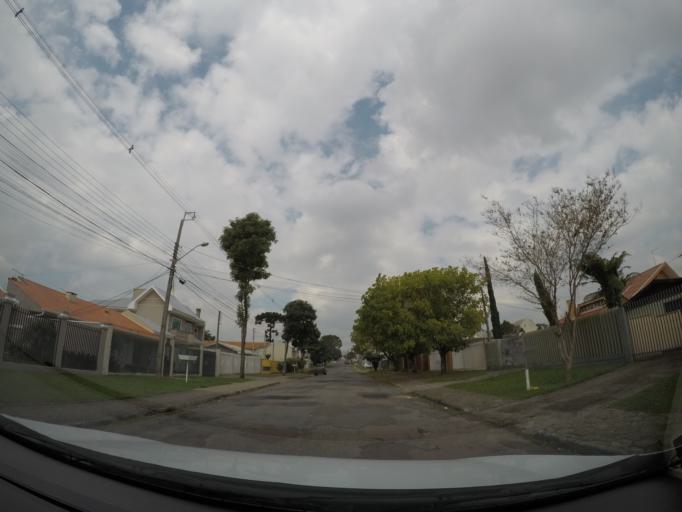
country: BR
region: Parana
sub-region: Sao Jose Dos Pinhais
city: Sao Jose dos Pinhais
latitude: -25.4926
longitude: -49.2530
